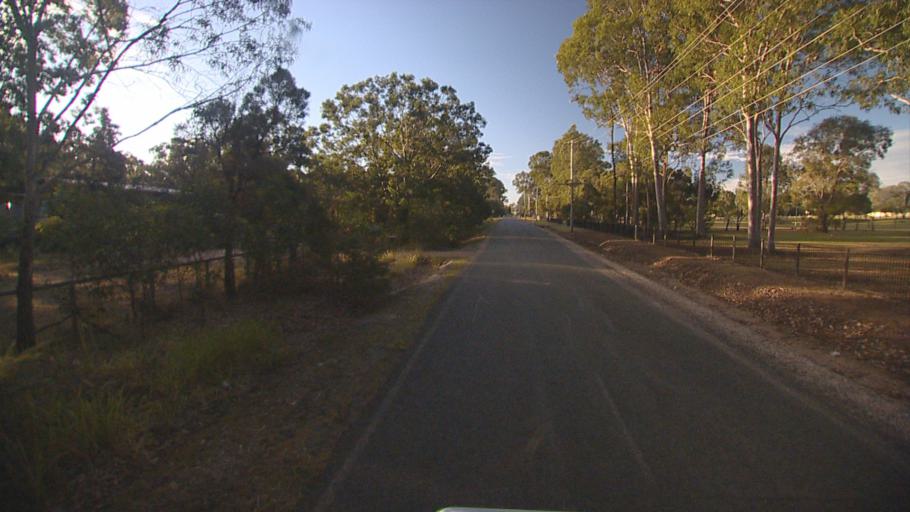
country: AU
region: Queensland
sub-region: Logan
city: Waterford West
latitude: -27.7234
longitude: 153.1417
